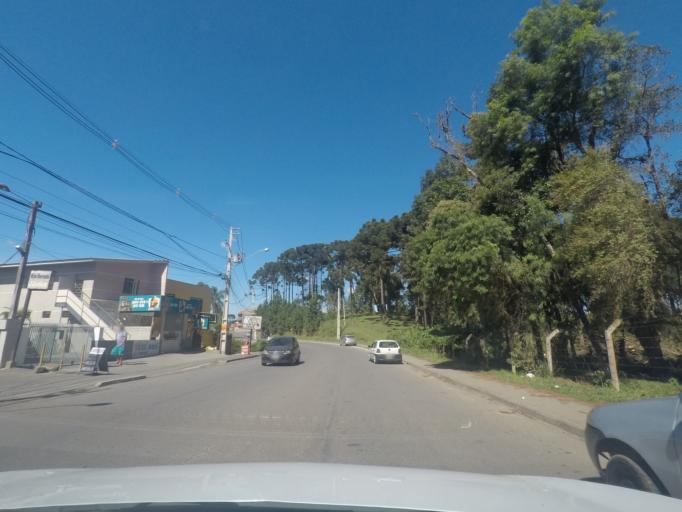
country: BR
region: Parana
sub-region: Almirante Tamandare
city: Almirante Tamandare
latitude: -25.3464
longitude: -49.2979
